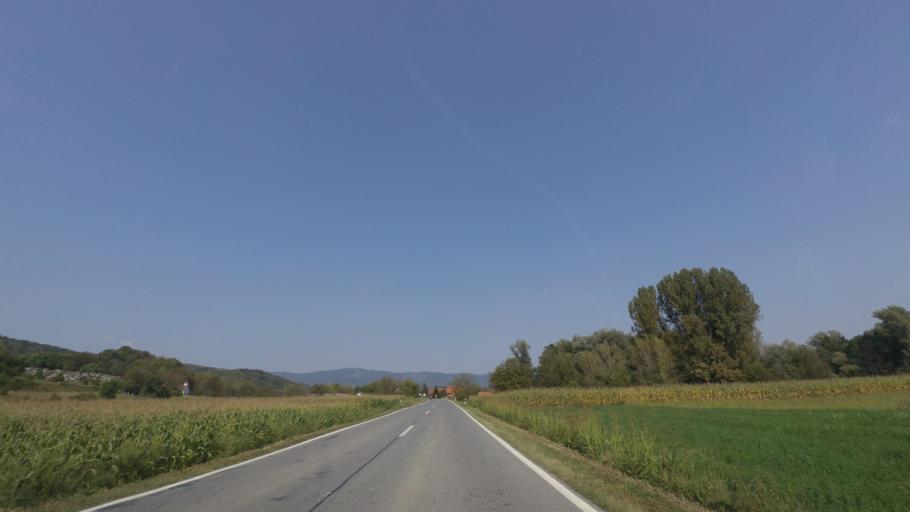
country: HR
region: Brodsko-Posavska
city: Resetari
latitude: 45.3619
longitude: 17.5395
